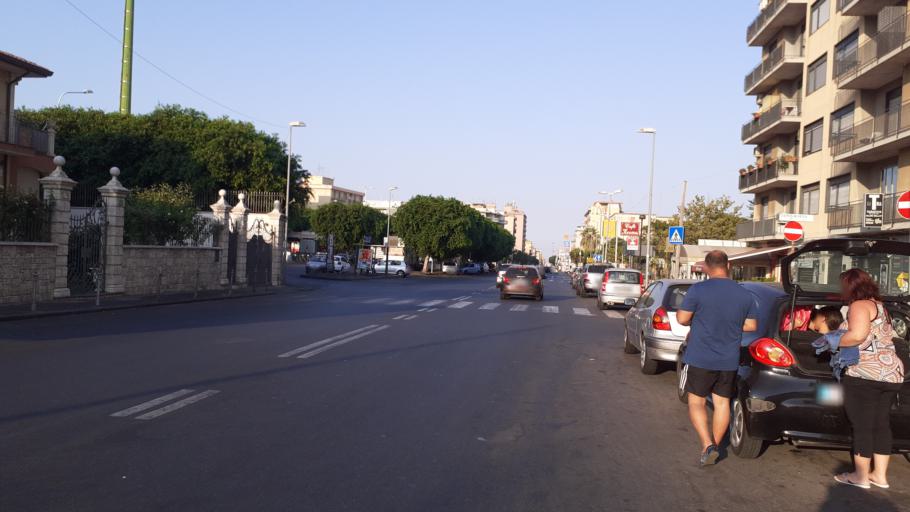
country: IT
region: Sicily
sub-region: Catania
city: Misterbianco
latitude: 37.5074
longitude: 15.0490
